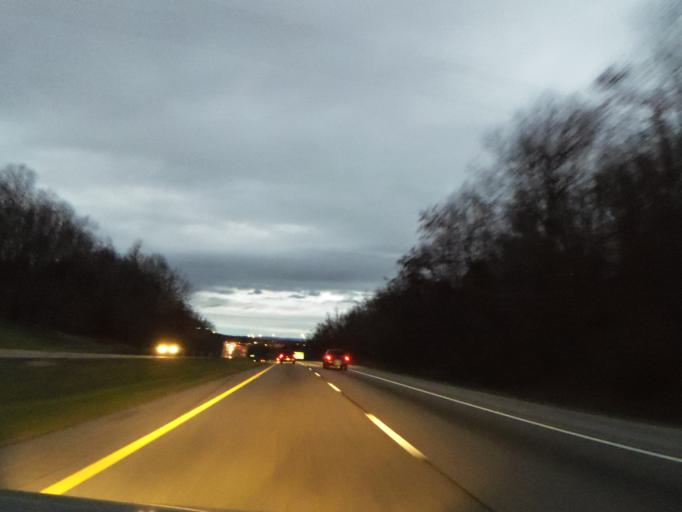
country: US
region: Tennessee
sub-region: Washington County
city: Gray
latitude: 36.3999
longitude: -82.4641
